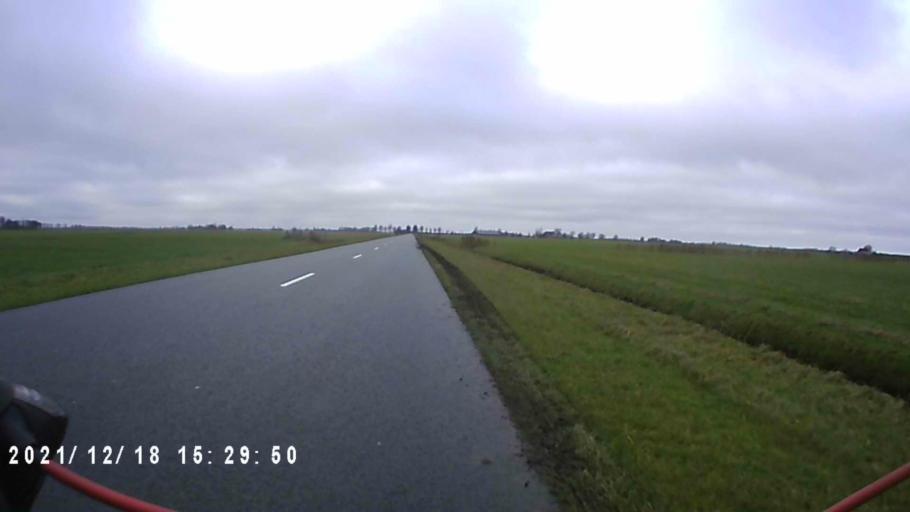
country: NL
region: Friesland
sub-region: Gemeente Dongeradeel
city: Anjum
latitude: 53.3354
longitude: 6.1404
